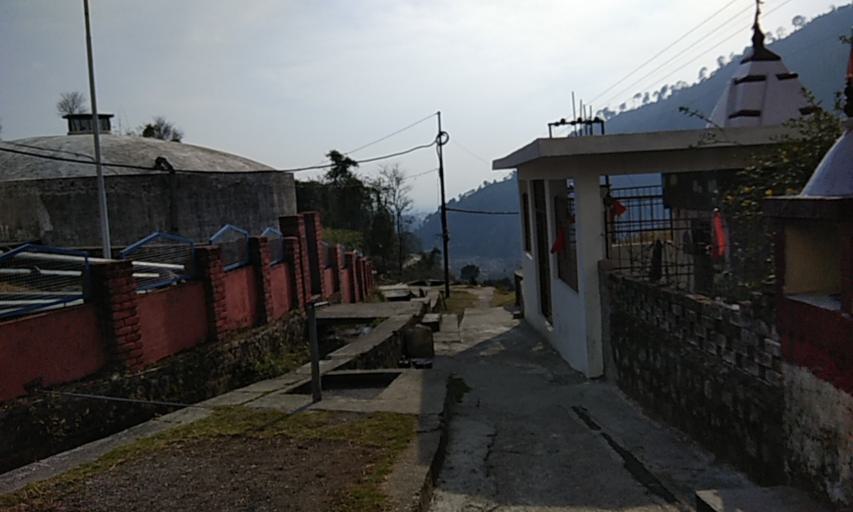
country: IN
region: Himachal Pradesh
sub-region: Kangra
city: Palampur
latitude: 32.1422
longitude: 76.5388
